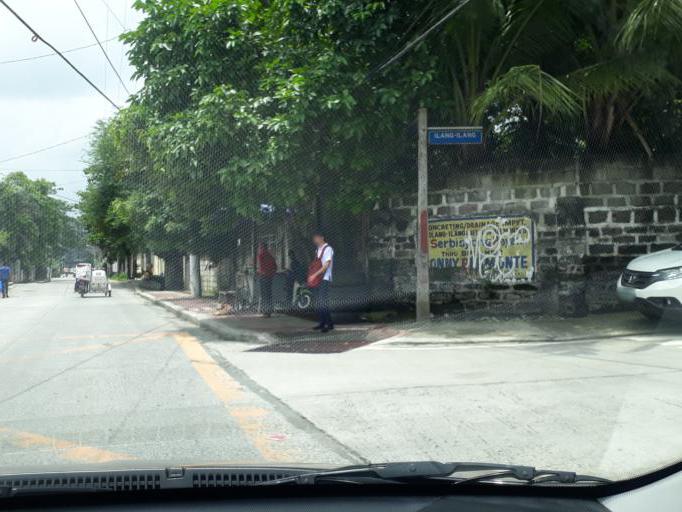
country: PH
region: Metro Manila
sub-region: San Juan
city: San Juan
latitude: 14.6222
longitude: 121.0390
